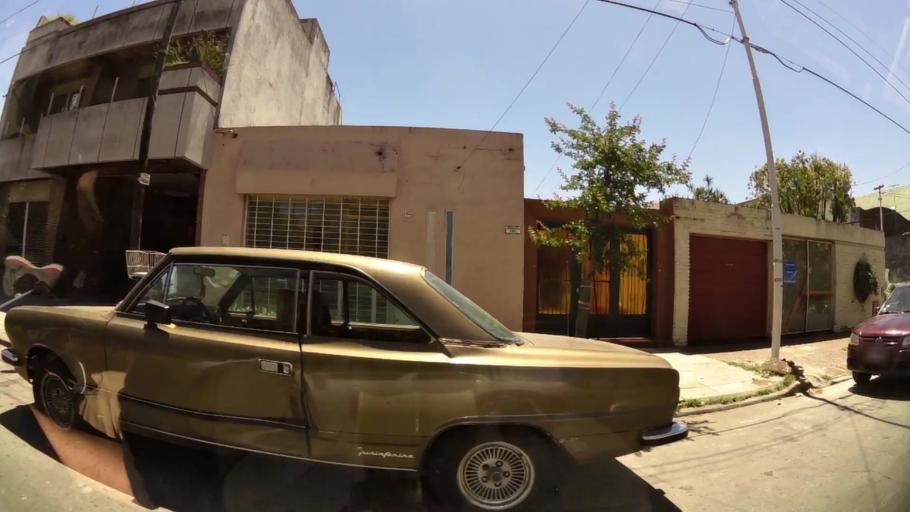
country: AR
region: Buenos Aires
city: Caseros
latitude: -34.5980
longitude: -58.5379
